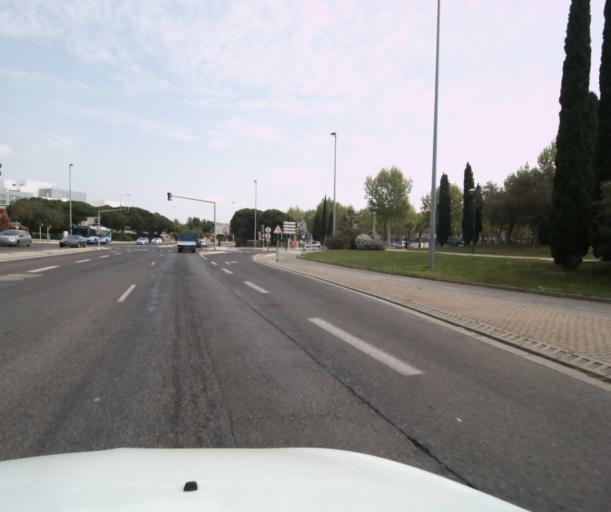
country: FR
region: Provence-Alpes-Cote d'Azur
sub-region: Departement du Var
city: La Garde
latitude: 43.1326
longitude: 6.0167
